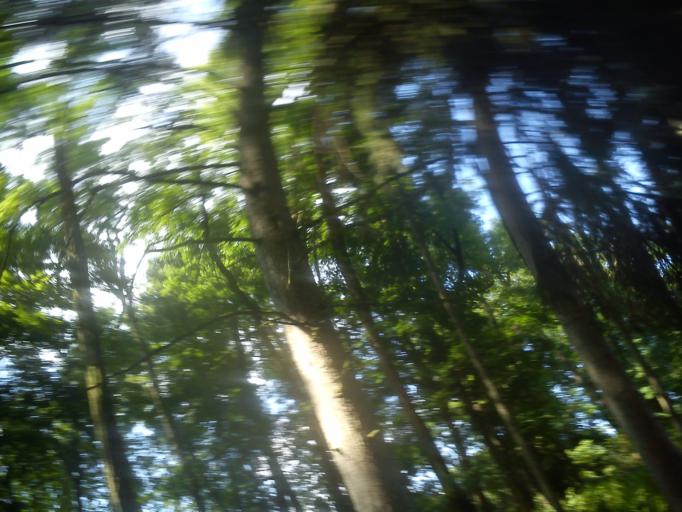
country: CZ
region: South Moravian
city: Sokolnice
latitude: 49.1211
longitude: 16.7265
